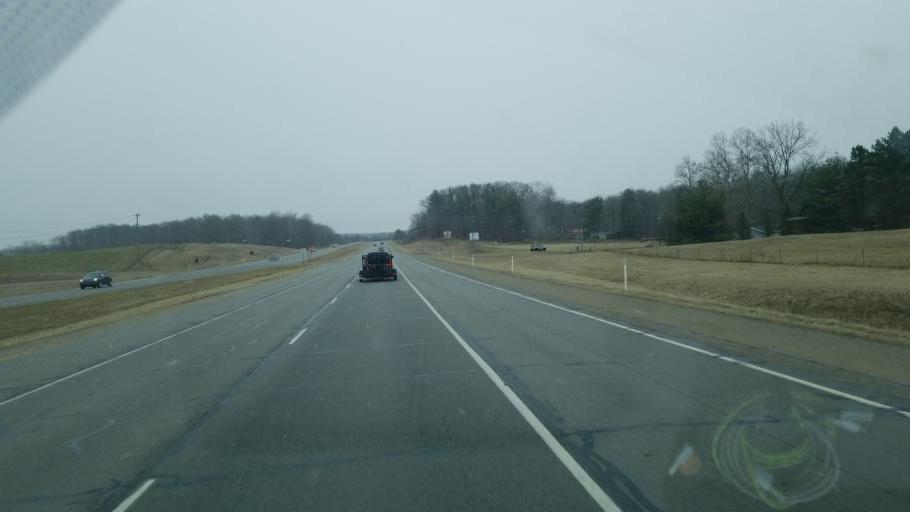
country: US
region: Indiana
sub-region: Miami County
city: Peru
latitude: 40.8001
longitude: -86.0297
